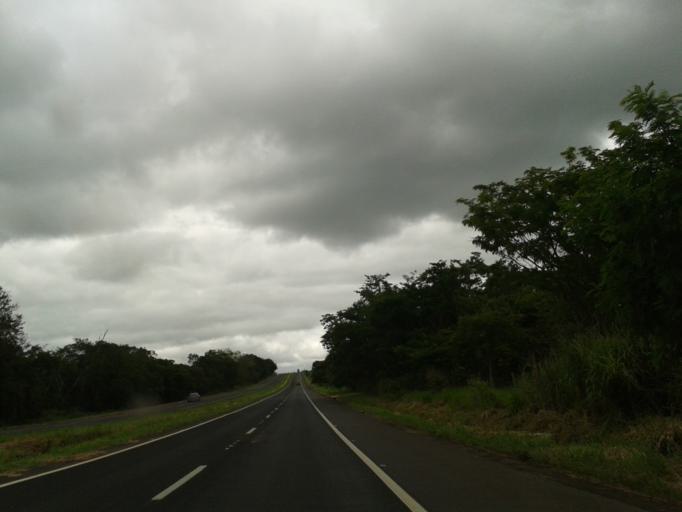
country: BR
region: Minas Gerais
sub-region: Monte Alegre De Minas
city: Monte Alegre de Minas
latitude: -18.8594
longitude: -48.7710
